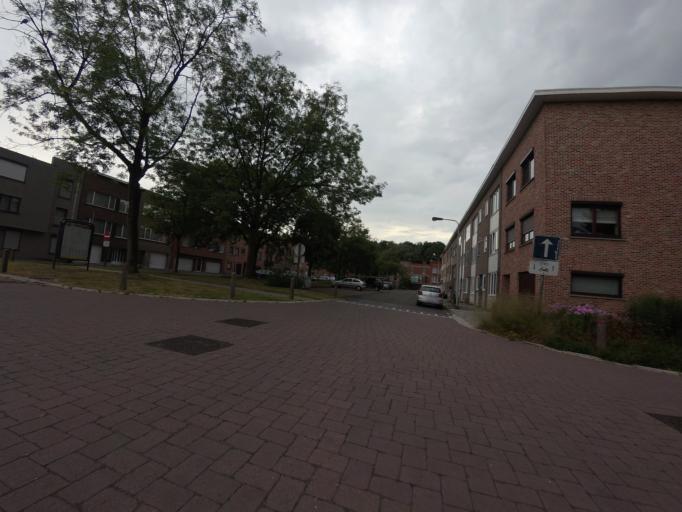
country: BE
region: Flanders
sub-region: Provincie Antwerpen
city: Edegem
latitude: 51.1609
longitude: 4.4195
